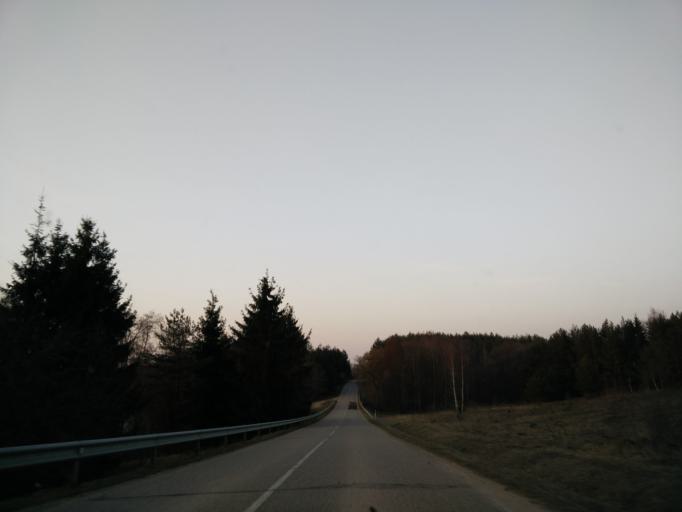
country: LT
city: Trakai
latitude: 54.6905
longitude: 24.9594
